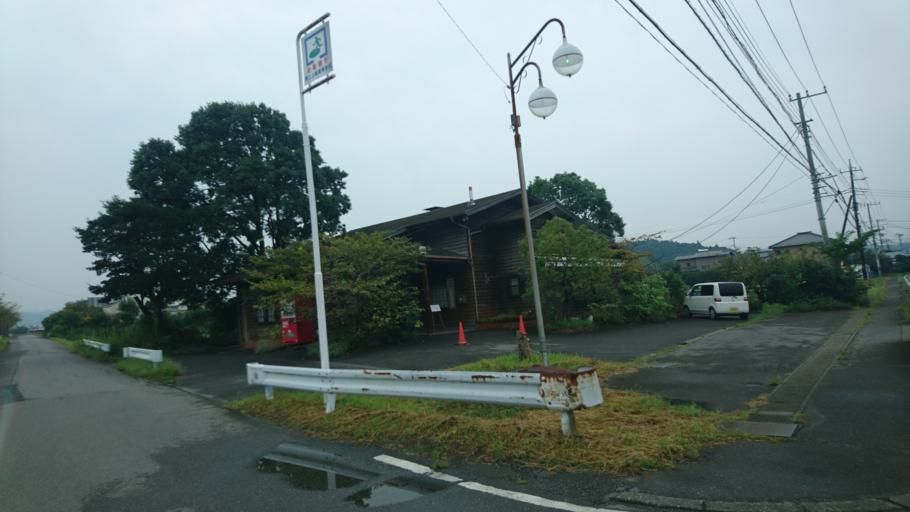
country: JP
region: Chiba
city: Kimitsu
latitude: 35.3078
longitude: 139.9594
